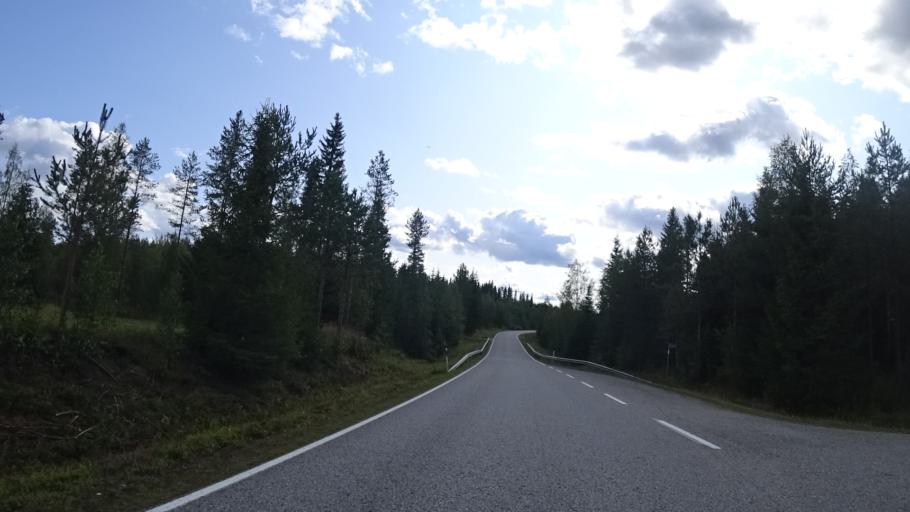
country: RU
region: Republic of Karelia
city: Vyartsilya
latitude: 62.2676
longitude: 30.7824
